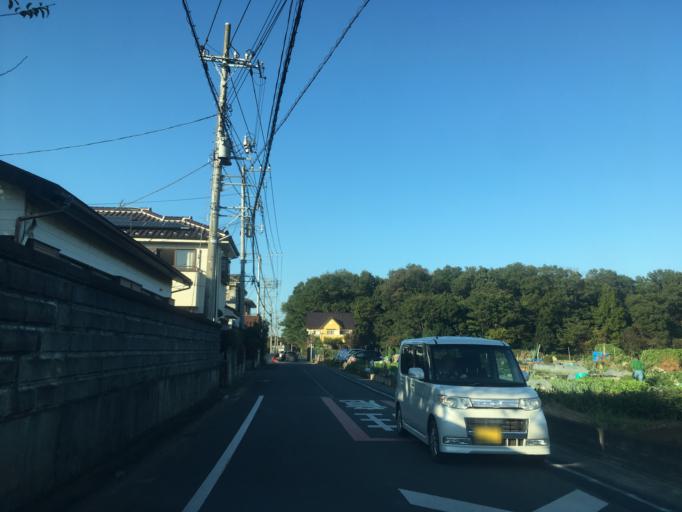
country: JP
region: Saitama
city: Tokorozawa
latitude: 35.8134
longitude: 139.4396
